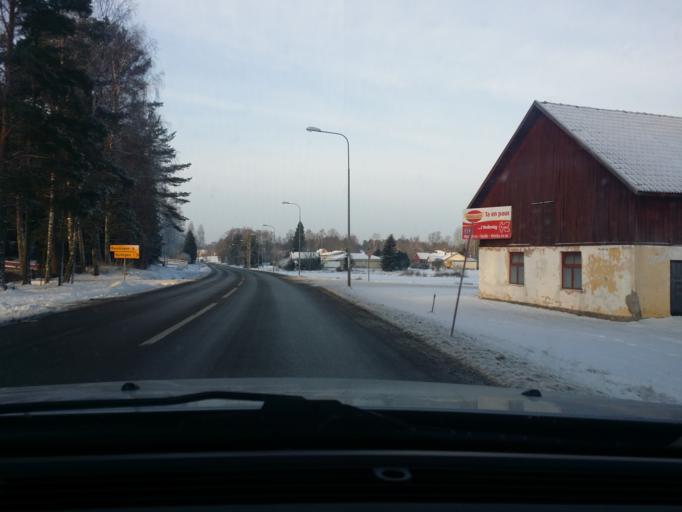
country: SE
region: OErebro
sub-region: Lindesbergs Kommun
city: Frovi
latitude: 59.5237
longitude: 15.3056
